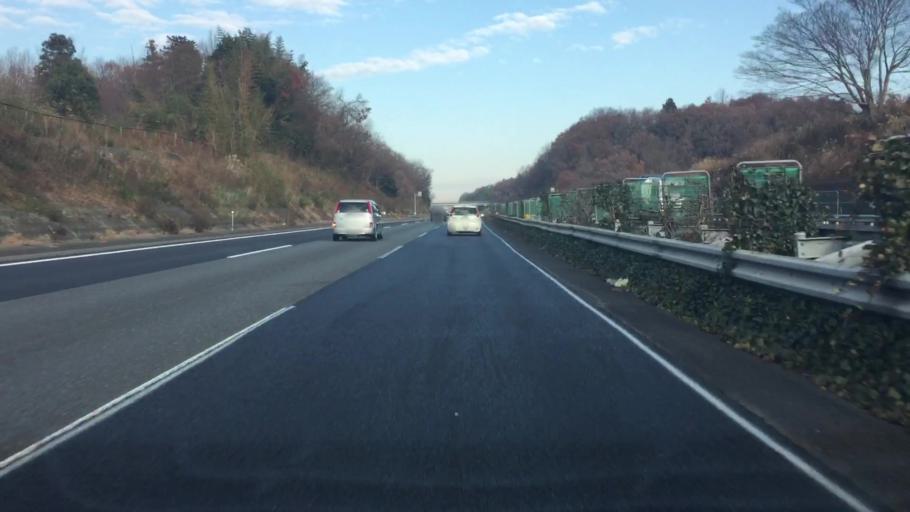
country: JP
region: Saitama
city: Ogawa
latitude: 36.0927
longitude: 139.2858
